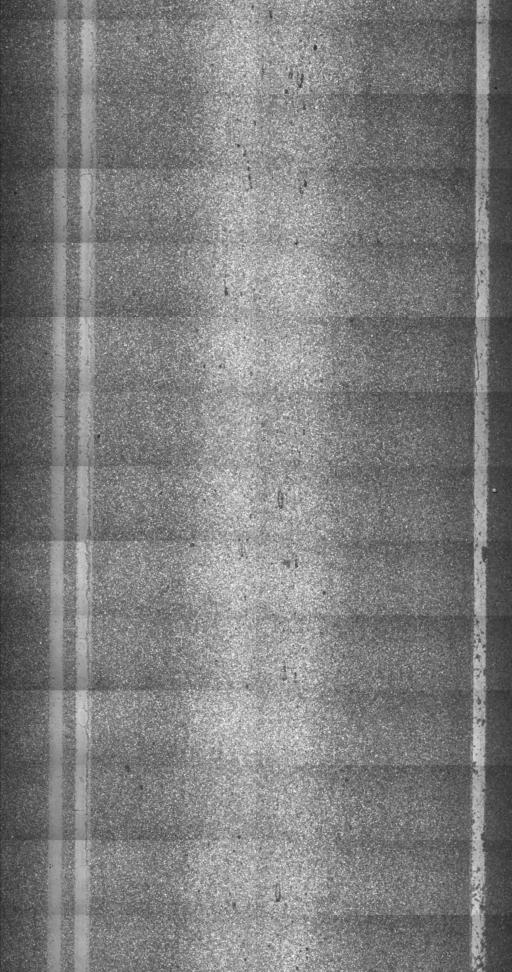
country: US
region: New York
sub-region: Washington County
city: Granville
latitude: 43.3448
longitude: -73.1773
